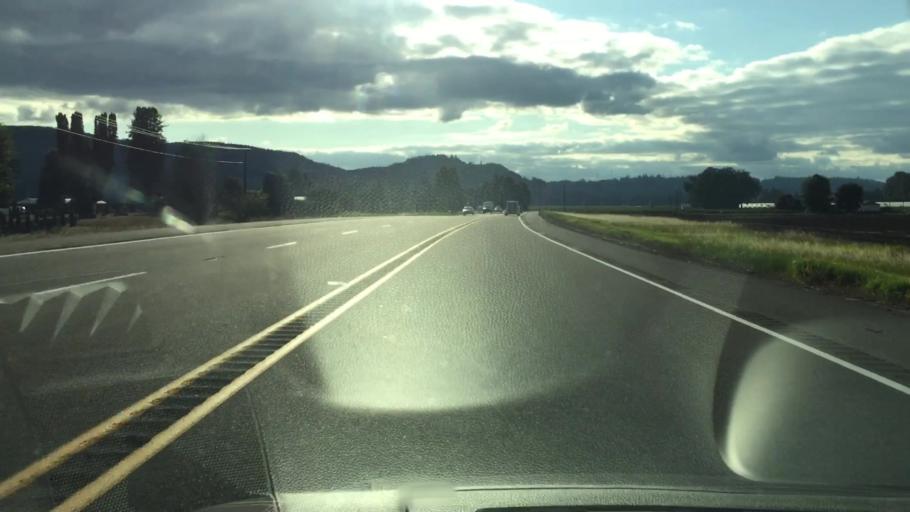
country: US
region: Washington
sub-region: Lewis County
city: Morton
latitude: 46.5330
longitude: -122.5118
